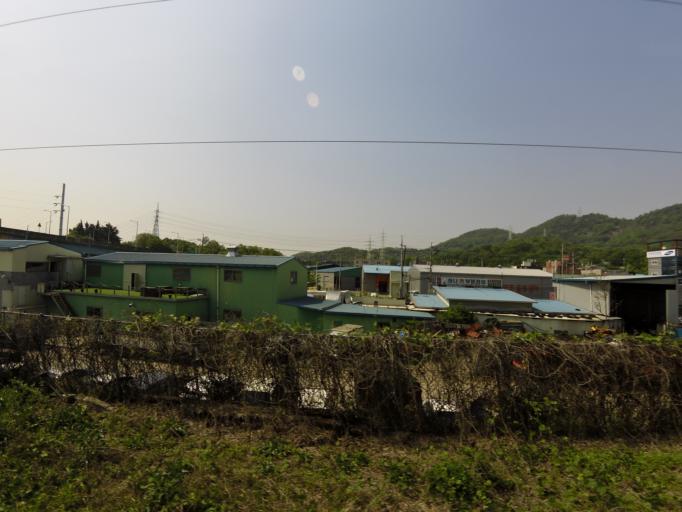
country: KR
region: Daegu
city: Daegu
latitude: 35.8821
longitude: 128.5336
